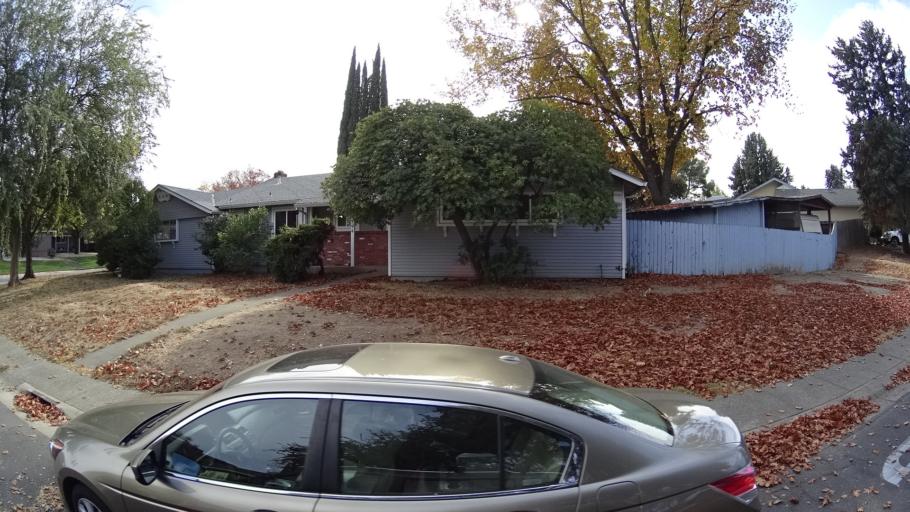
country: US
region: California
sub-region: Sacramento County
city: Fair Oaks
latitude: 38.6667
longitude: -121.2769
